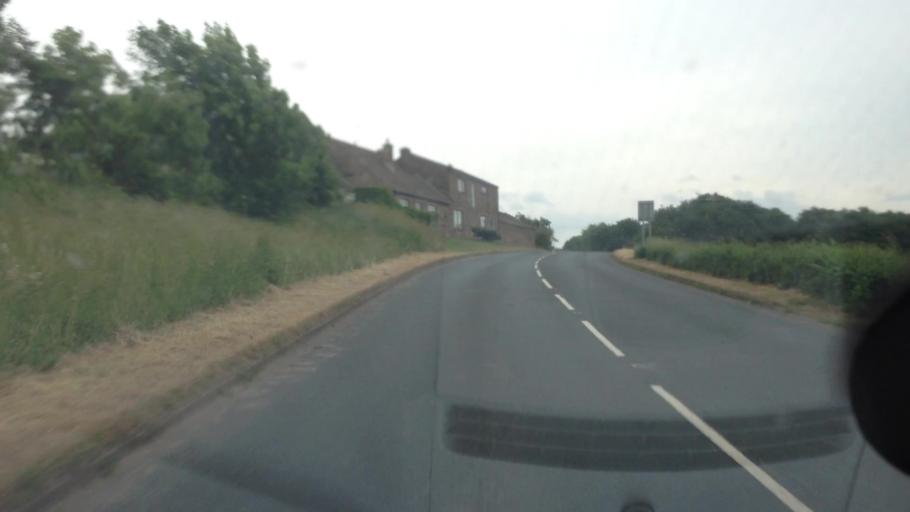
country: GB
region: England
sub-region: City and Borough of Wakefield
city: Woolley
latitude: 53.6137
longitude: -1.5358
